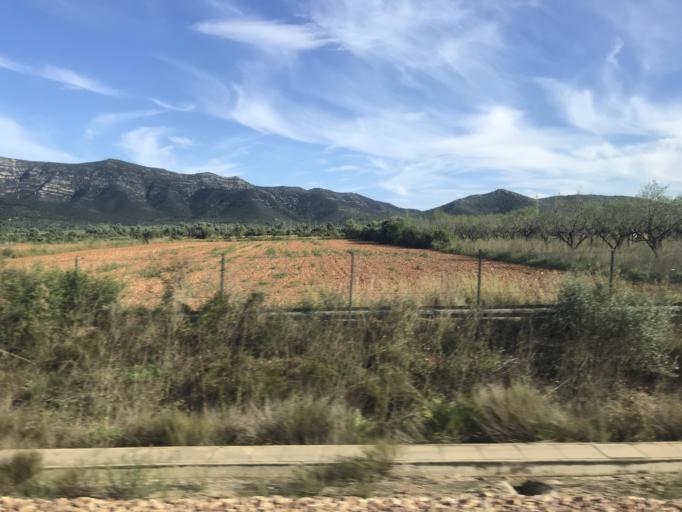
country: ES
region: Catalonia
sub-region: Provincia de Tarragona
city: Ulldecona
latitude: 40.6199
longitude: 0.4751
